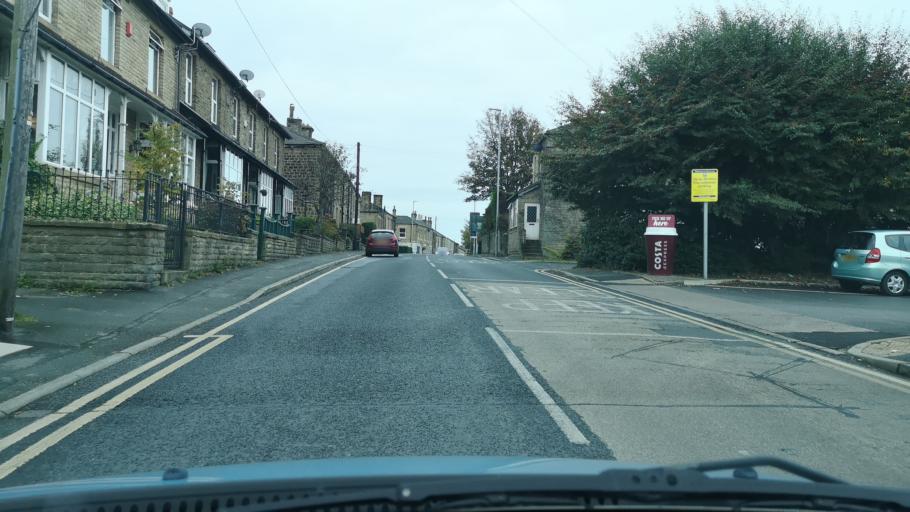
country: GB
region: England
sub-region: Kirklees
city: Heckmondwike
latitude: 53.7293
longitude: -1.6835
